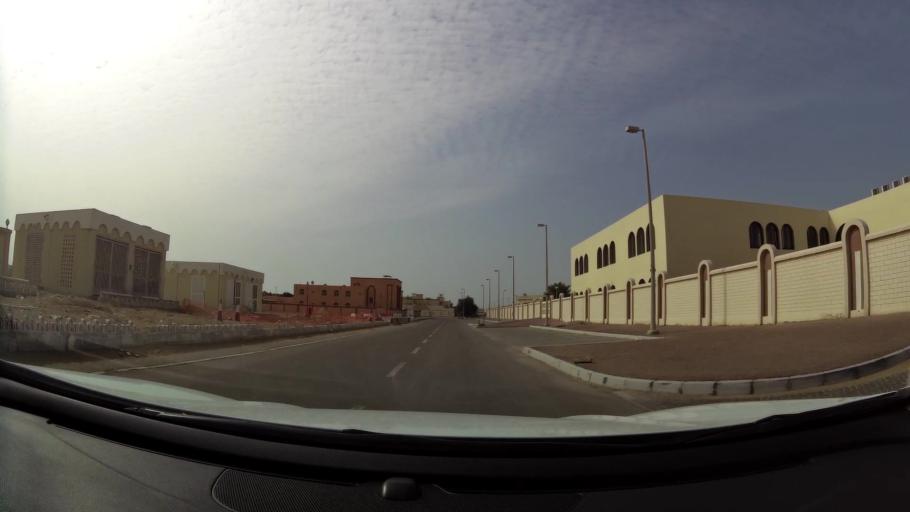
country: AE
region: Abu Dhabi
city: Abu Dhabi
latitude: 24.5947
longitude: 54.7007
